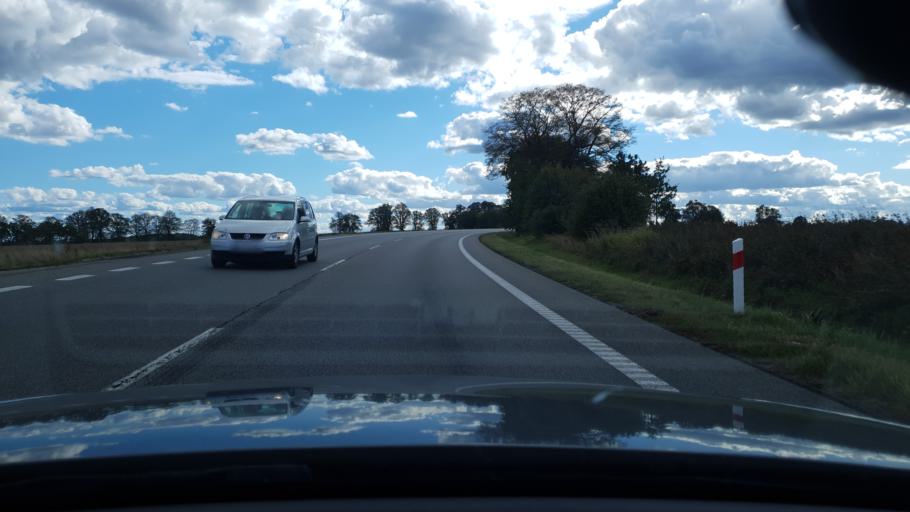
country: PL
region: Pomeranian Voivodeship
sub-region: Powiat pucki
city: Zelistrzewo
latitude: 54.6760
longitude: 18.3752
